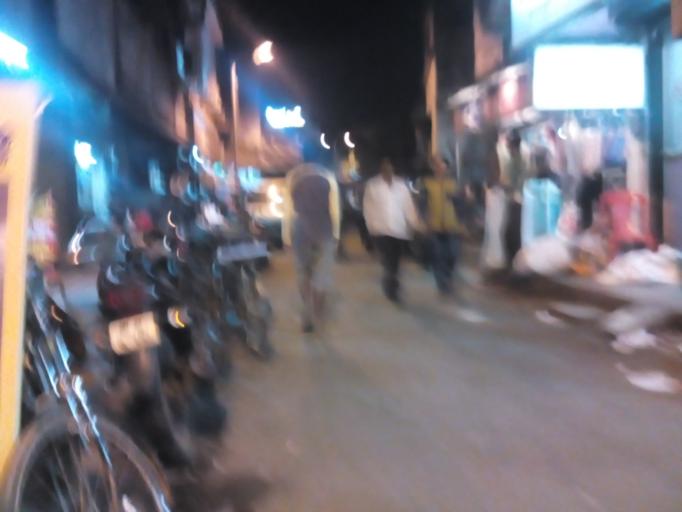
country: IN
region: Maharashtra
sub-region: Thane
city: Bhayandar
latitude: 19.3109
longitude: 72.8534
